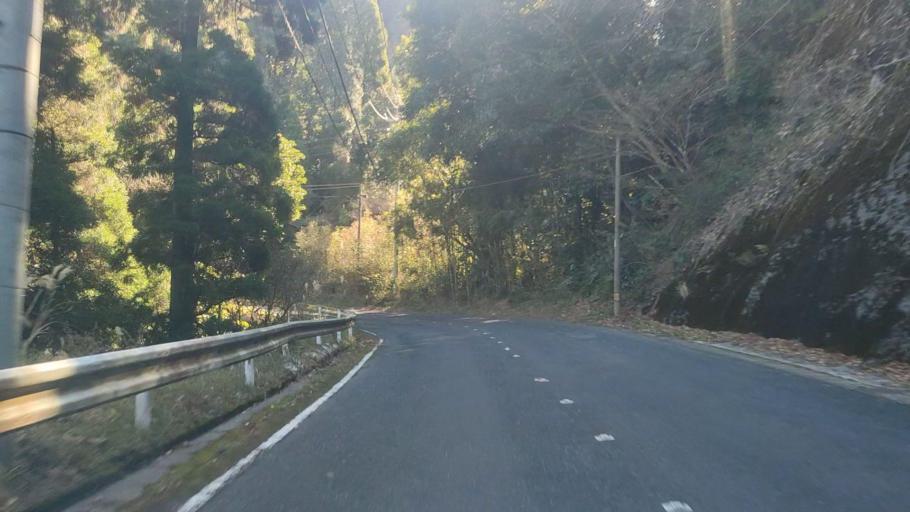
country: JP
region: Kagoshima
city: Kokubu-matsuki
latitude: 31.6702
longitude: 130.8339
